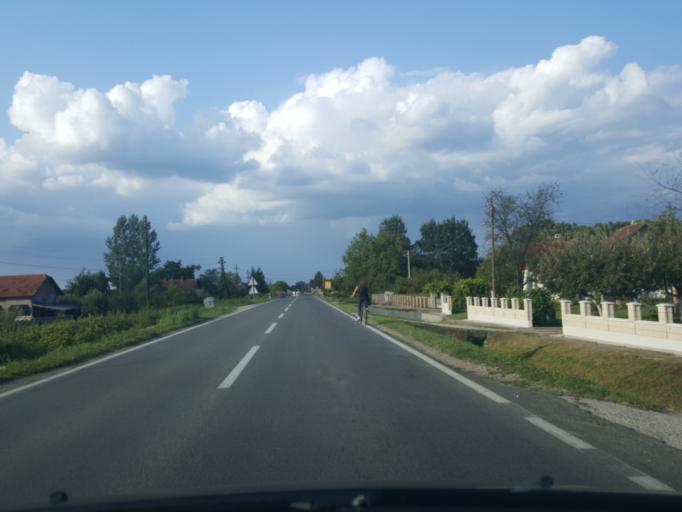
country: RS
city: Lipnicki Sor
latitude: 44.6122
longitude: 19.2622
